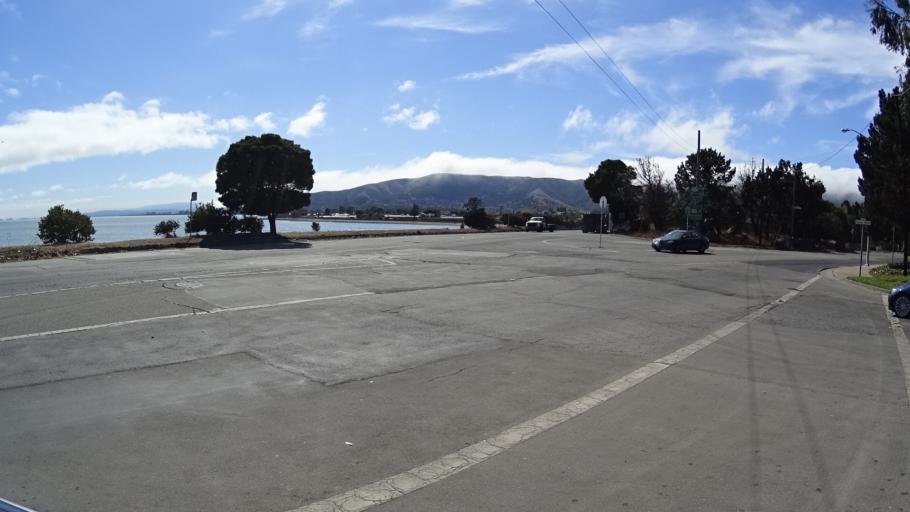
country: US
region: California
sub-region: San Mateo County
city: Brisbane
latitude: 37.7094
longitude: -122.3926
